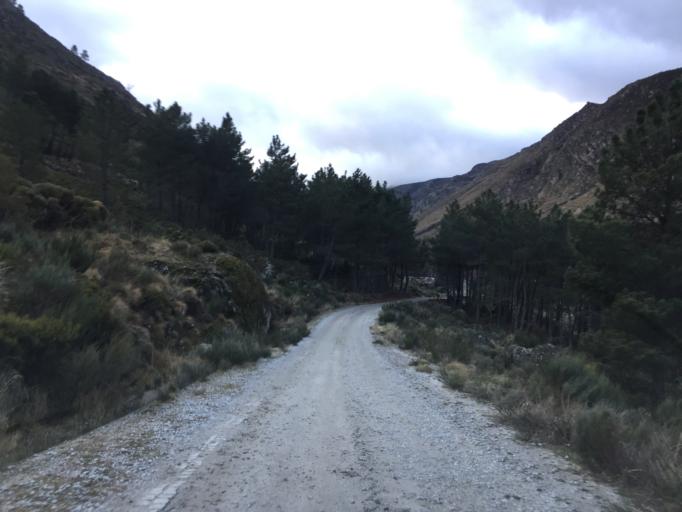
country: PT
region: Guarda
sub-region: Manteigas
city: Manteigas
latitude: 40.3583
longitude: -7.5563
